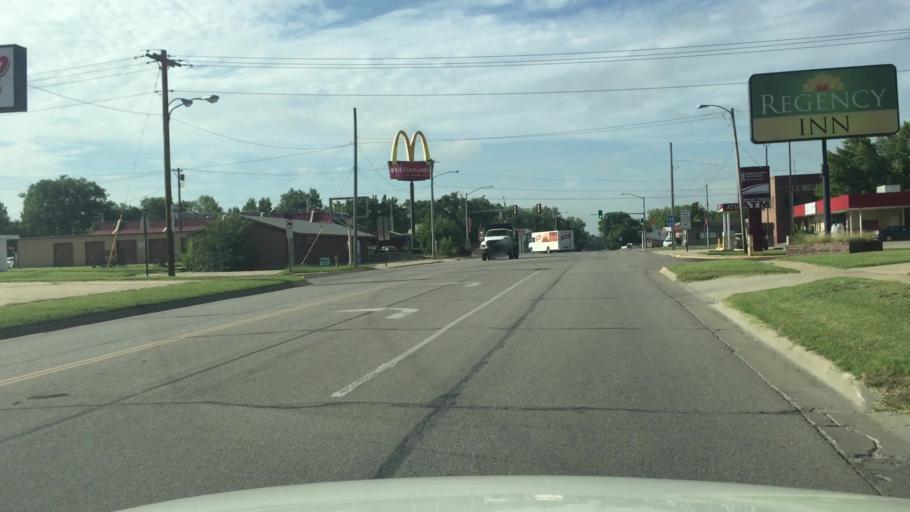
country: US
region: Kansas
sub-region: Allen County
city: Iola
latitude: 37.9226
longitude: -95.4091
